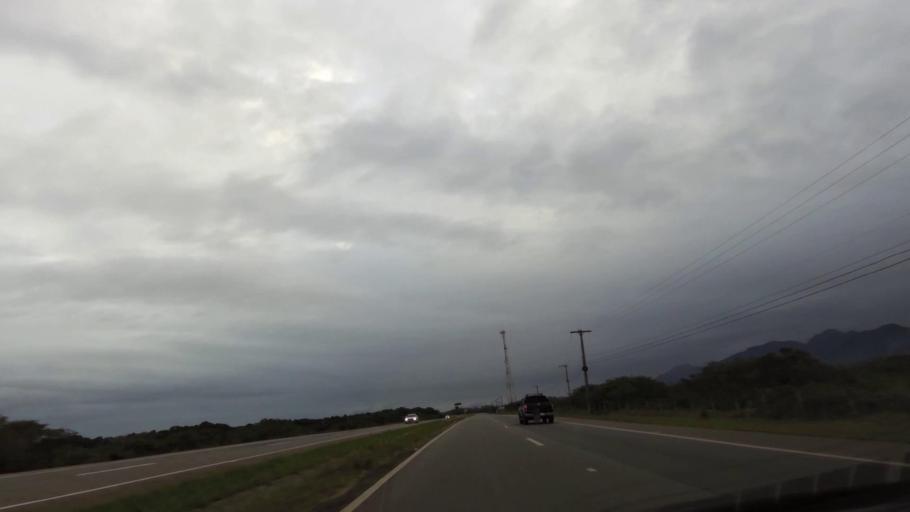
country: BR
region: Espirito Santo
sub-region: Guarapari
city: Guarapari
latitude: -20.5820
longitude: -40.4186
